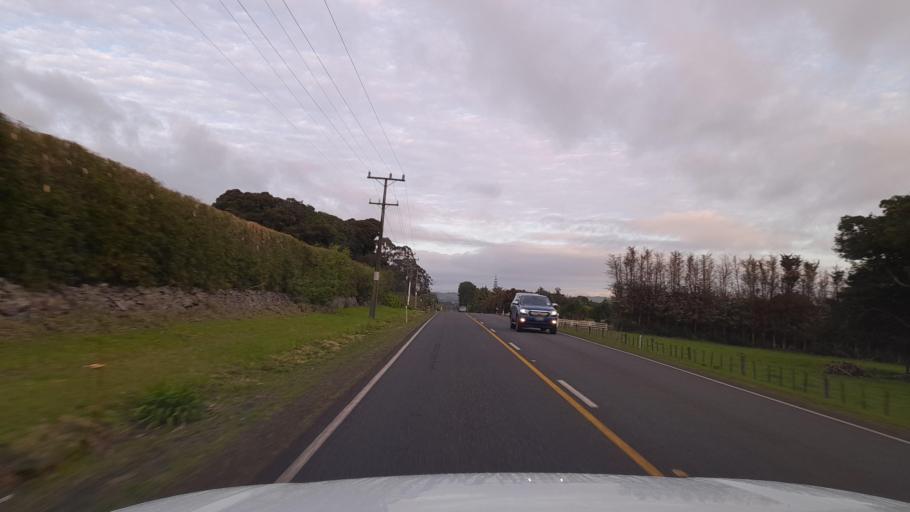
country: NZ
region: Northland
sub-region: Whangarei
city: Maungatapere
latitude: -35.7472
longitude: 174.1593
